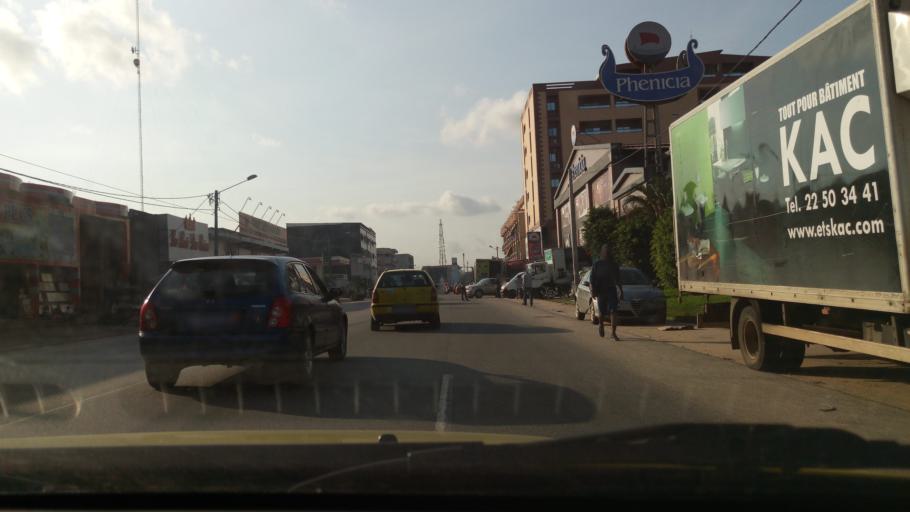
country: CI
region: Lagunes
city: Abobo
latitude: 5.3965
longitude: -3.9772
